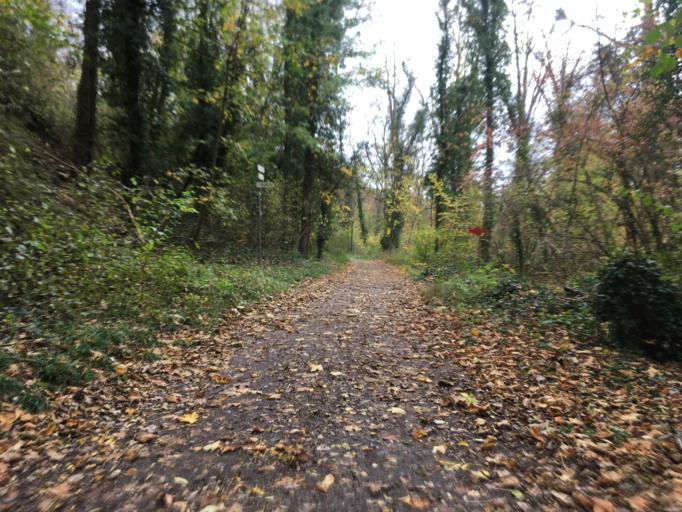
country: DE
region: Baden-Wuerttemberg
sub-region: Freiburg Region
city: Sasbach
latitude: 48.1111
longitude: 7.5863
